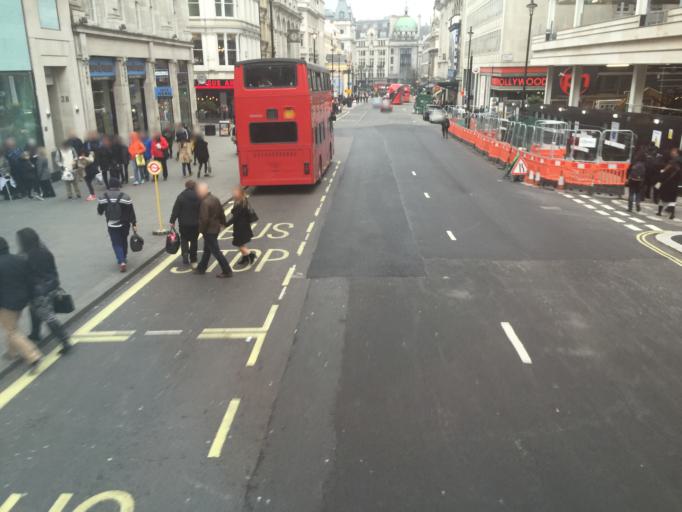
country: GB
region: England
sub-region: Greater London
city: London
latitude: 51.5096
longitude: -0.1328
